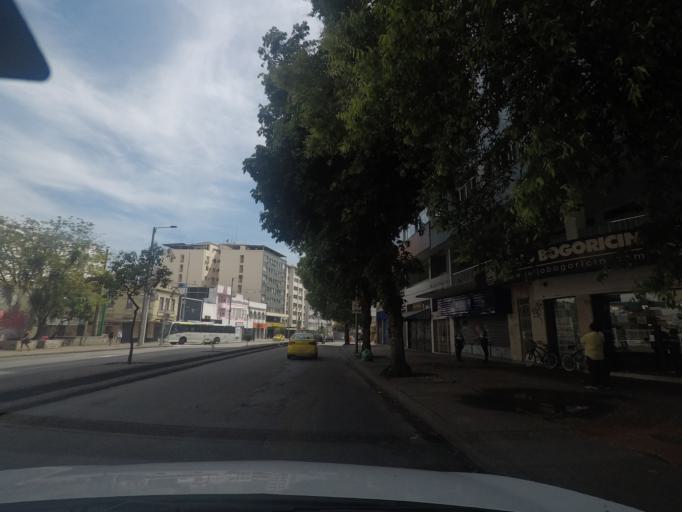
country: BR
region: Rio de Janeiro
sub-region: Rio De Janeiro
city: Rio de Janeiro
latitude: -22.9263
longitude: -43.2351
